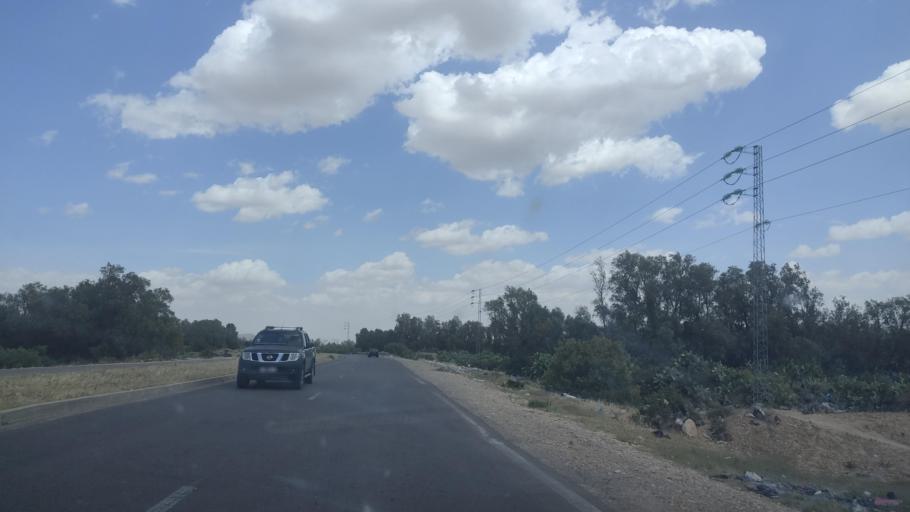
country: TN
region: Al Qasrayn
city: Kasserine
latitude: 35.1979
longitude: 8.8668
